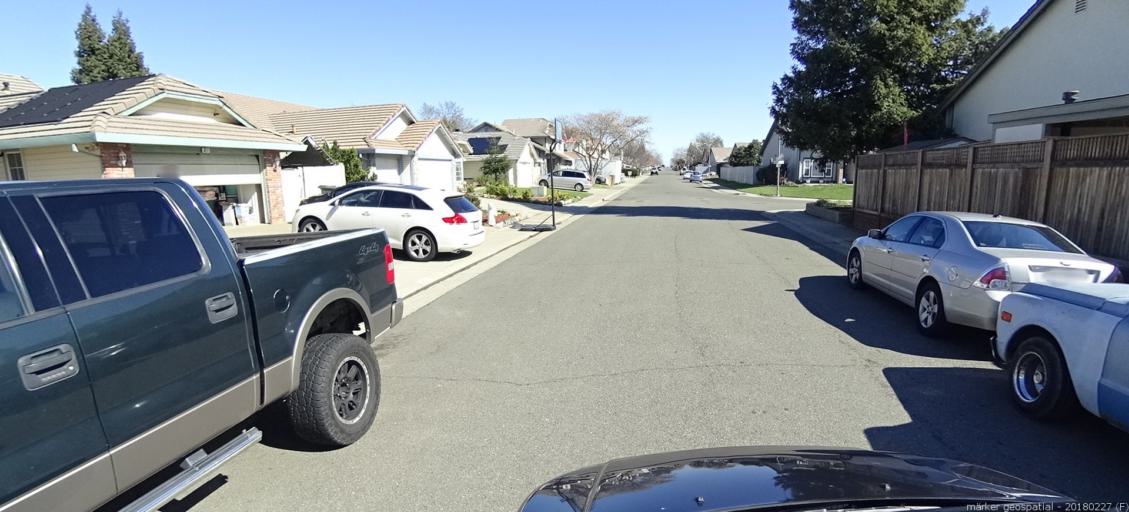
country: US
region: California
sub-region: Sacramento County
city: North Highlands
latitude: 38.7279
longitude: -121.3887
